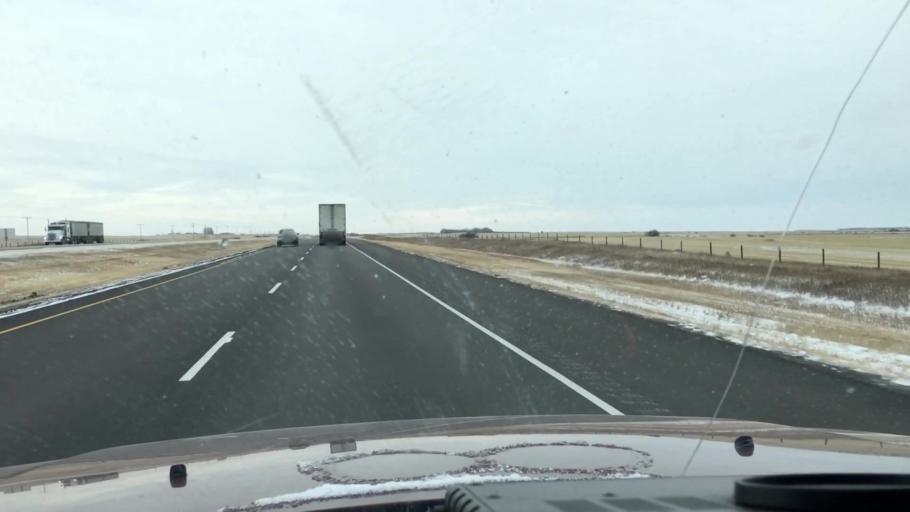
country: CA
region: Saskatchewan
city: Saskatoon
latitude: 51.7997
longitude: -106.4893
